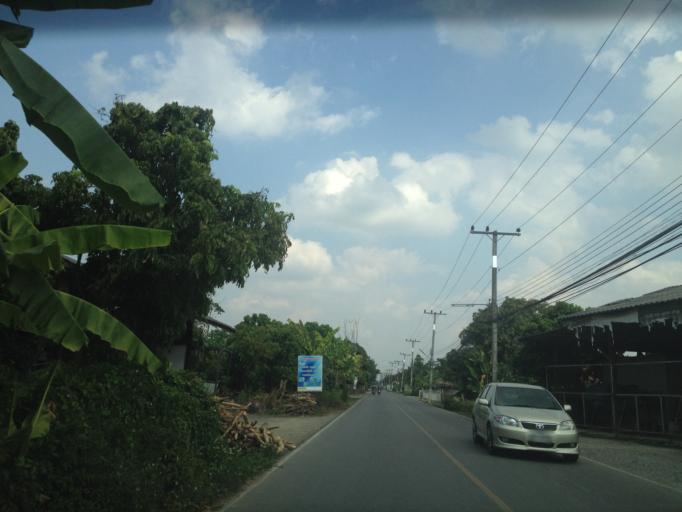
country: TH
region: Chiang Mai
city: Saraphi
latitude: 18.6878
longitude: 98.9978
